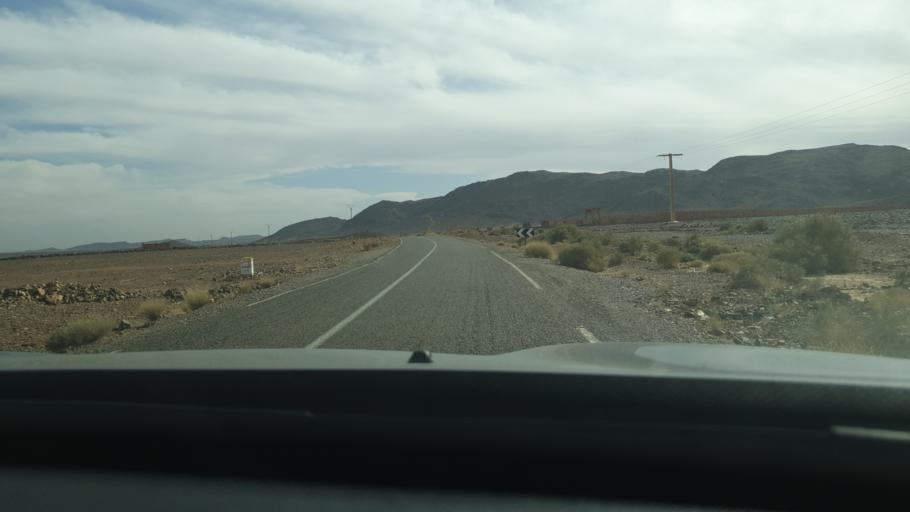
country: MA
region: Meknes-Tafilalet
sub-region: Errachidia
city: Fezna
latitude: 31.5295
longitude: -4.6381
